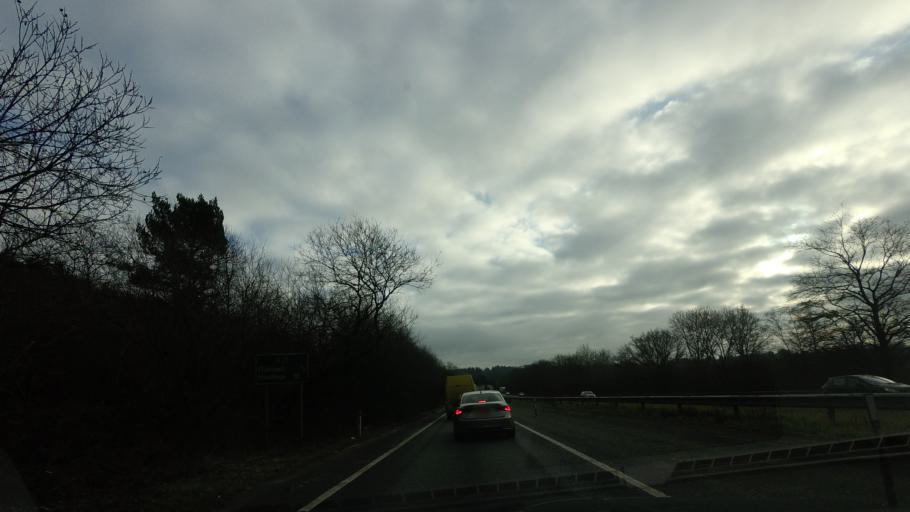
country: GB
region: England
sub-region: Kent
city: Hawkhurst
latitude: 51.0623
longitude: 0.4429
